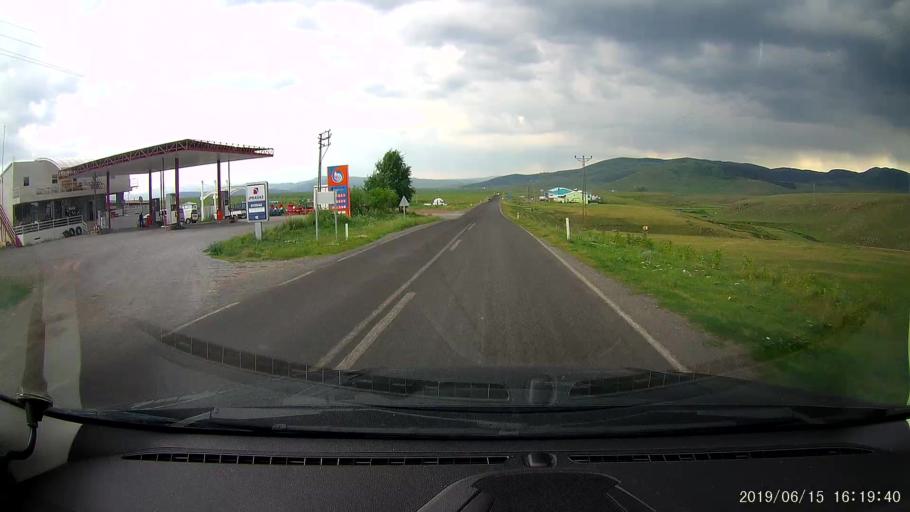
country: TR
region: Ardahan
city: Hanak
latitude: 41.2261
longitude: 42.8498
